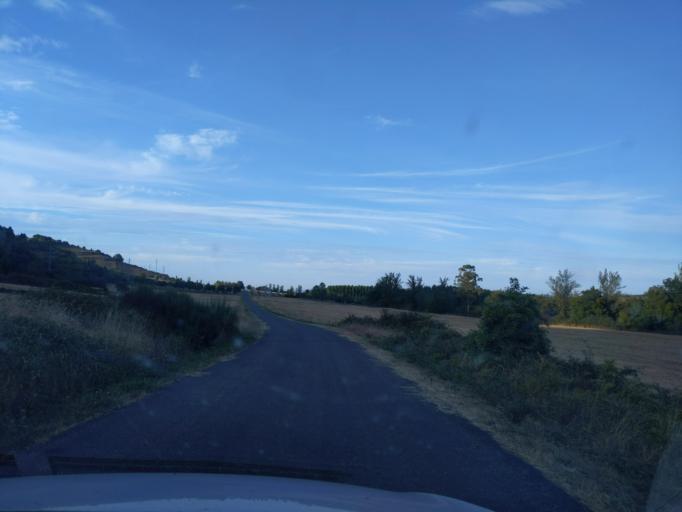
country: ES
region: La Rioja
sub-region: Provincia de La Rioja
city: Santurdejo
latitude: 42.3743
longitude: -2.9866
